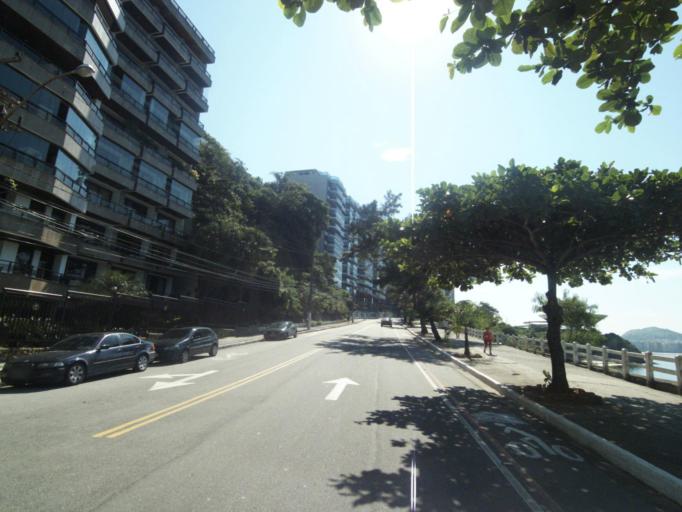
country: BR
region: Rio de Janeiro
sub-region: Niteroi
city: Niteroi
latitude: -22.9081
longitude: -43.1297
